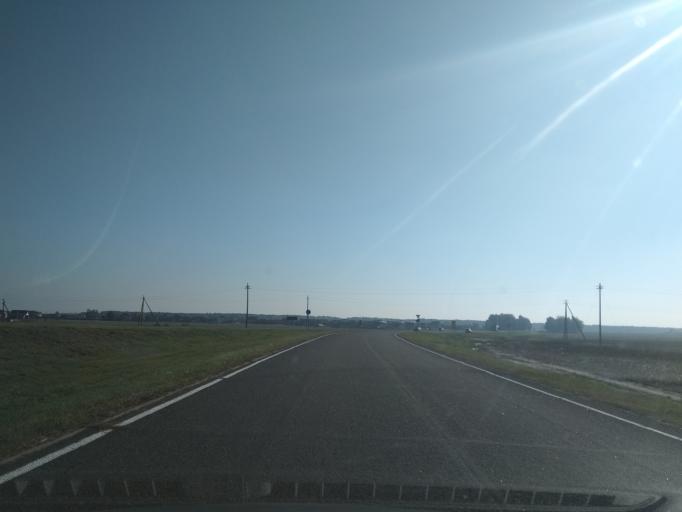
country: BY
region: Brest
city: Ivatsevichy
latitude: 52.6967
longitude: 25.3635
